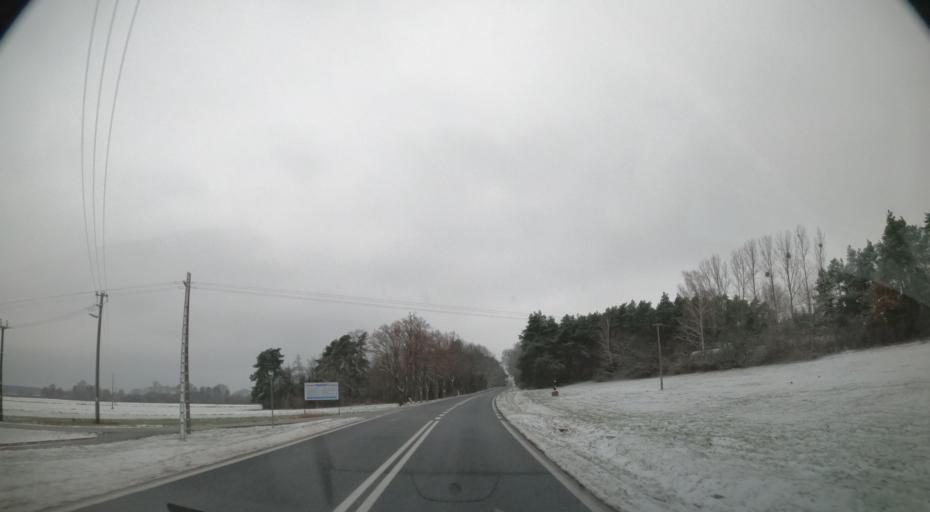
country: PL
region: Masovian Voivodeship
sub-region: Powiat plocki
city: Nowy Duninow
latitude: 52.5836
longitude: 19.5240
